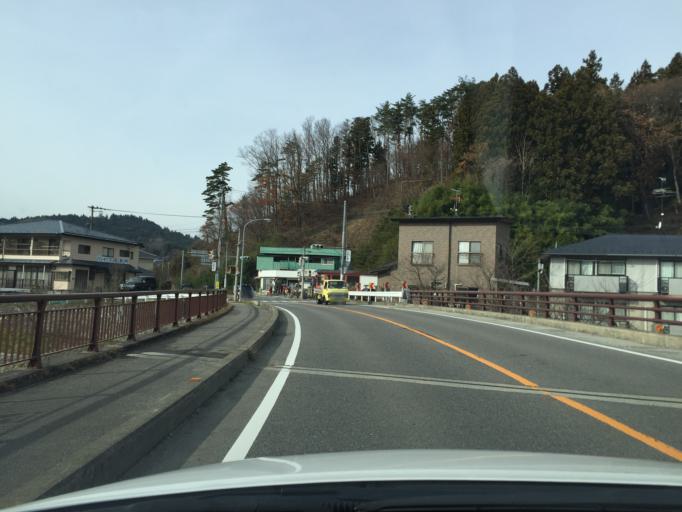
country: JP
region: Fukushima
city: Funehikimachi-funehiki
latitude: 37.4413
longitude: 140.5627
